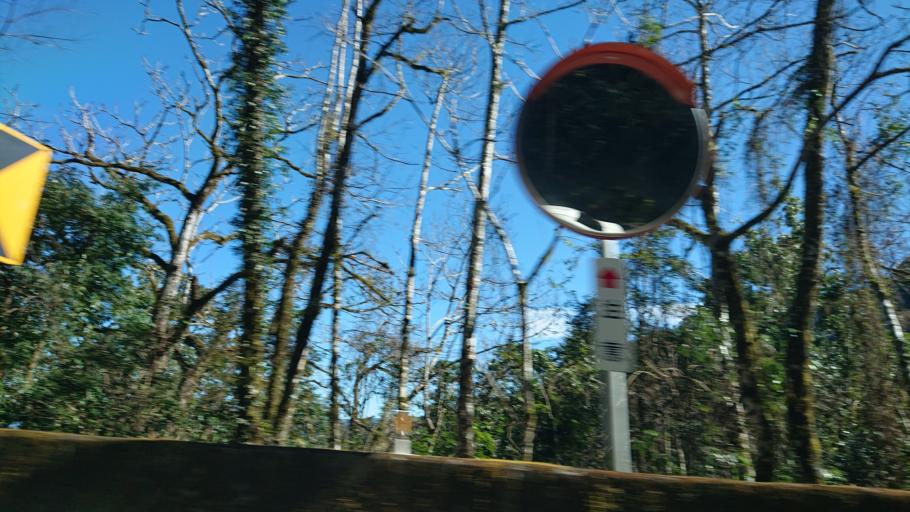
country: TW
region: Taiwan
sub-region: Hualien
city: Hualian
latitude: 24.4015
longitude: 121.3654
